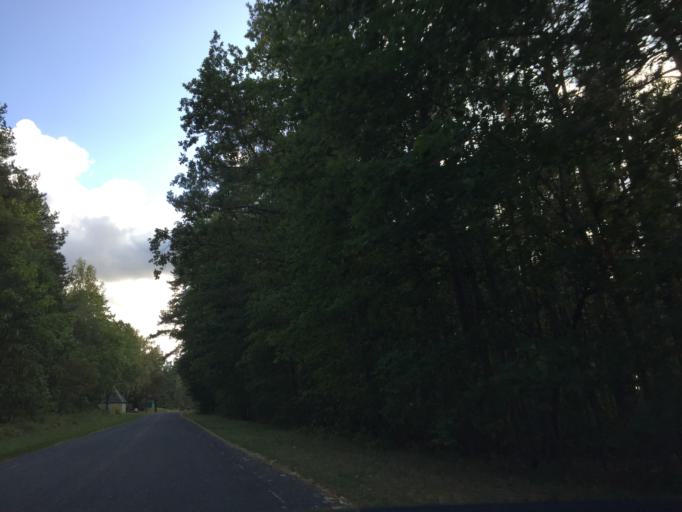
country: LV
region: Salacgrivas
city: Ainazi
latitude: 57.9158
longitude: 24.3857
